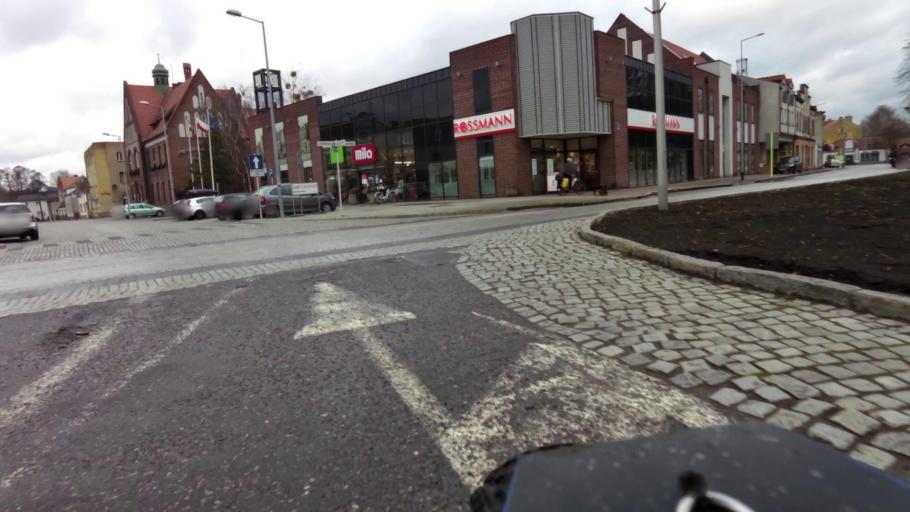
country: PL
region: Lubusz
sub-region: Powiat gorzowski
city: Witnica
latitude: 52.6729
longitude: 14.8976
